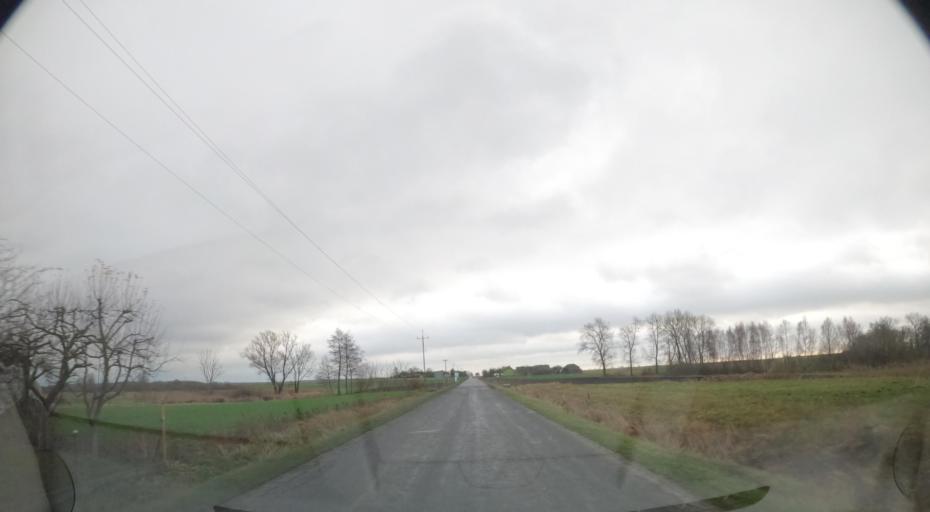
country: PL
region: Greater Poland Voivodeship
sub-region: Powiat pilski
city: Lobzenica
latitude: 53.2204
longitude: 17.3412
